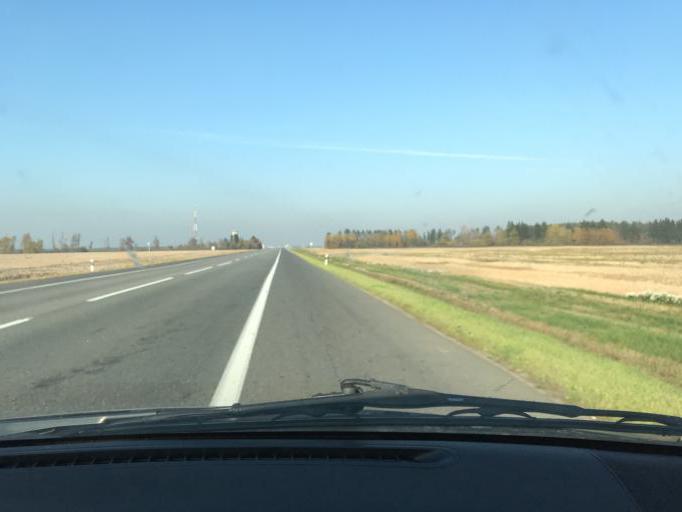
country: BY
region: Vitebsk
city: Orsha
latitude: 54.3412
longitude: 30.4461
